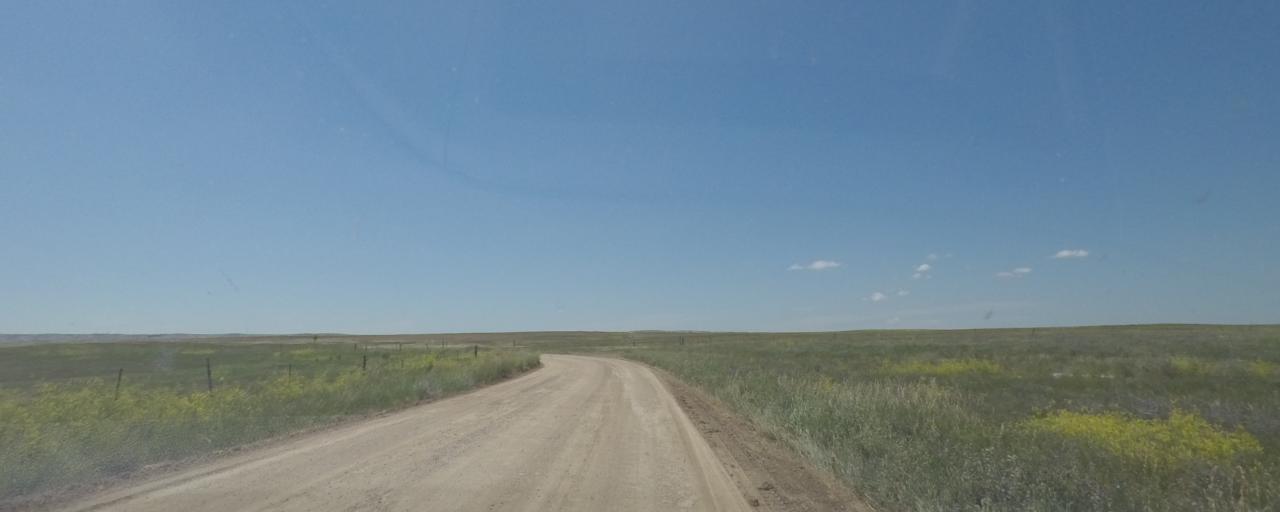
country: US
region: South Dakota
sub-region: Haakon County
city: Philip
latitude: 43.9367
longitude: -102.1573
